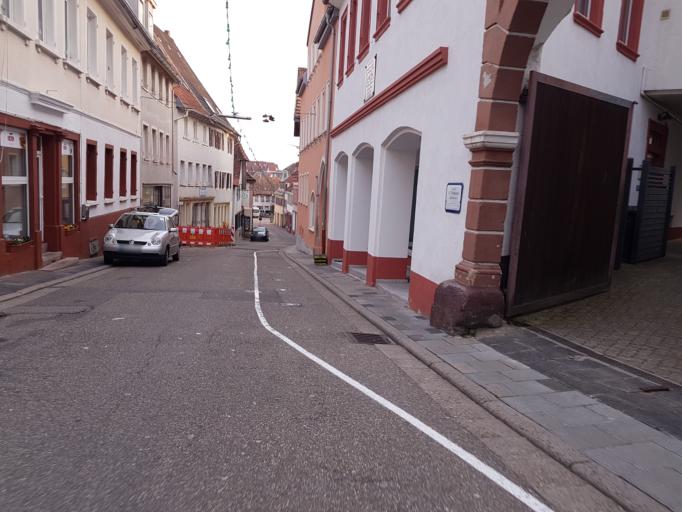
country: DE
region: Rheinland-Pfalz
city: Edenkoben
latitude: 49.2815
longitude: 8.1272
